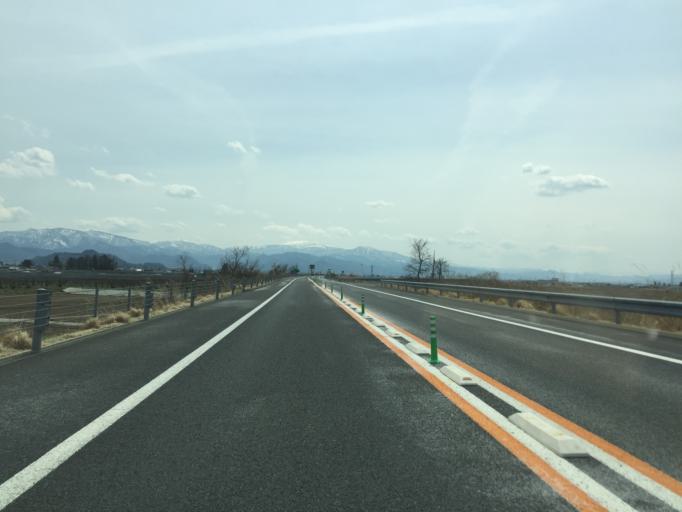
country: JP
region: Yamagata
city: Tendo
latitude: 38.3874
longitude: 140.3440
